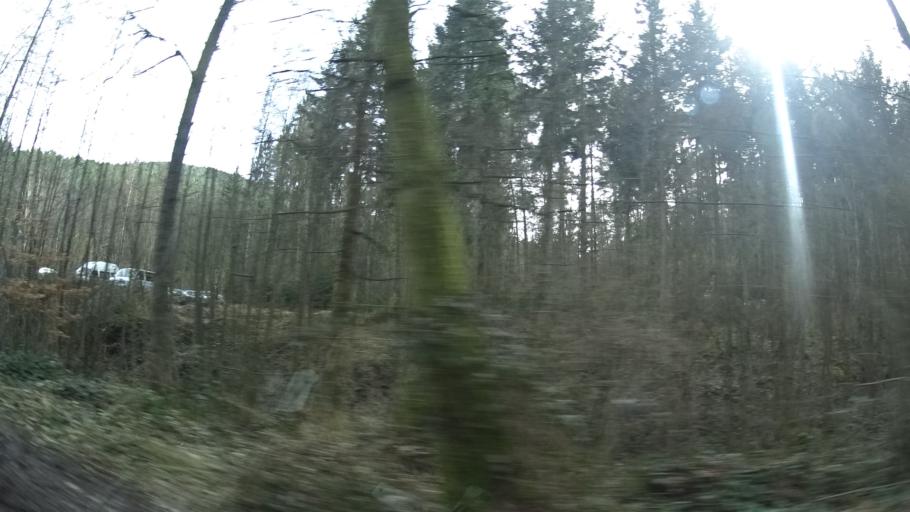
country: DE
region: Rheinland-Pfalz
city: Sankt Martin
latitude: 49.2948
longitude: 8.0554
